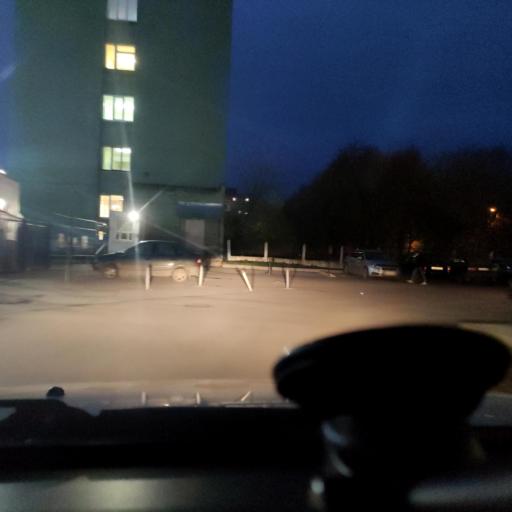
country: RU
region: Perm
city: Perm
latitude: 57.9636
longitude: 56.2365
